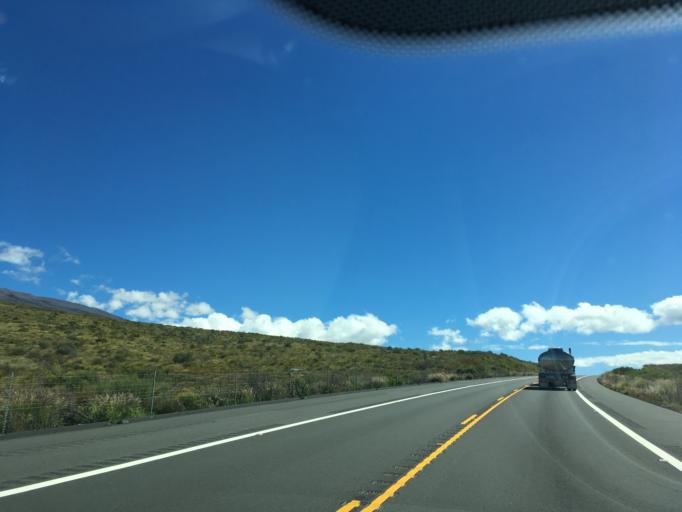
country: US
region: Hawaii
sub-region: Hawaii County
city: Waikoloa
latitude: 19.7774
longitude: -155.5952
